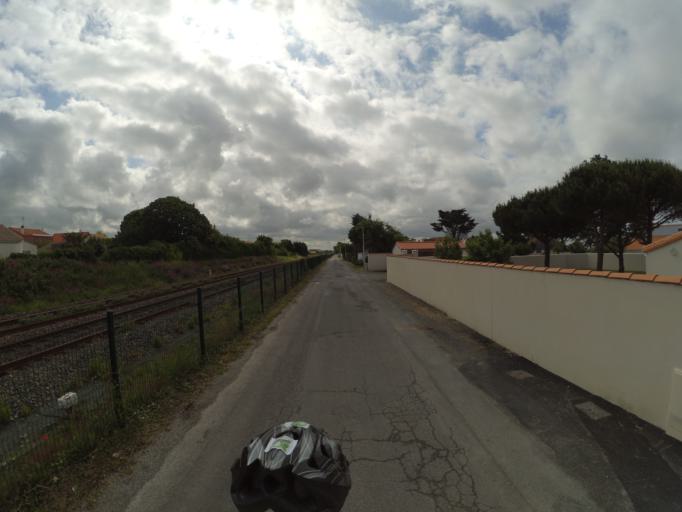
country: FR
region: Poitou-Charentes
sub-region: Departement de la Charente-Maritime
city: Angoulins
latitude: 46.0982
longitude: -1.1063
